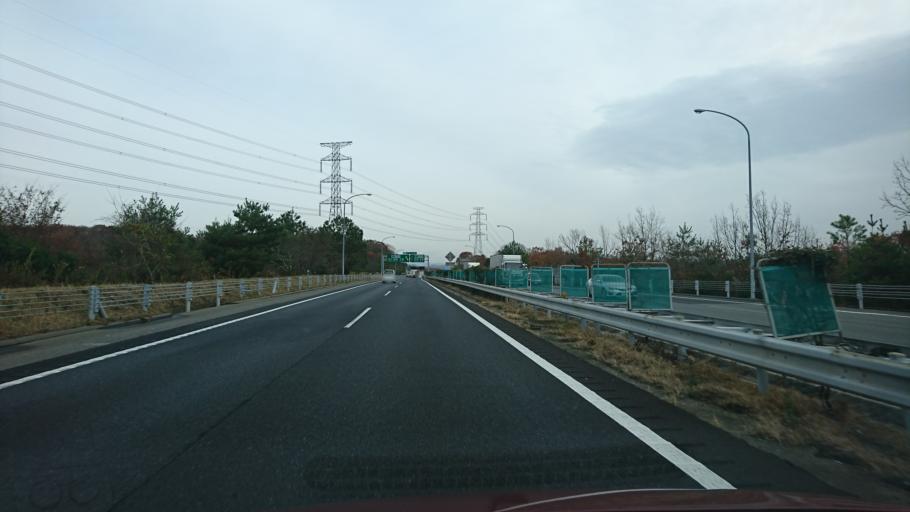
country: JP
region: Hyogo
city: Sandacho
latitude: 34.8434
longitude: 135.2034
